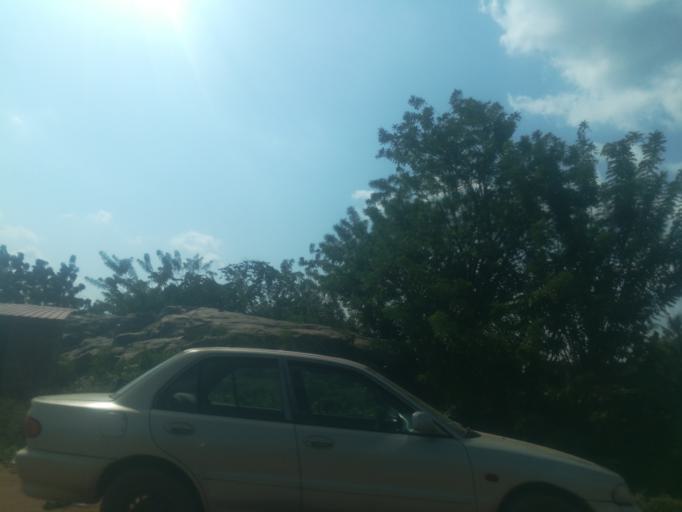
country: NG
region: Oyo
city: Moniya
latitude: 7.5349
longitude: 3.9118
